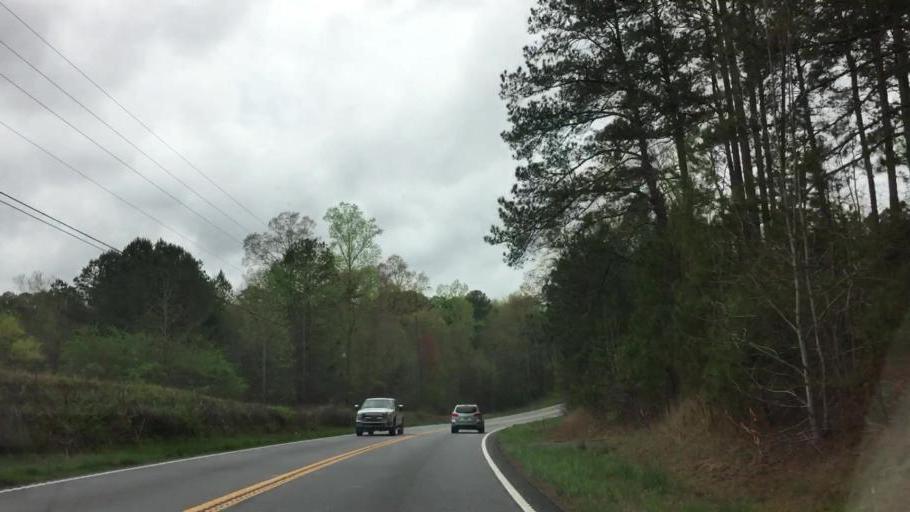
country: US
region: Georgia
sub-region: Cherokee County
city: Holly Springs
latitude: 34.2171
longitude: -84.6073
